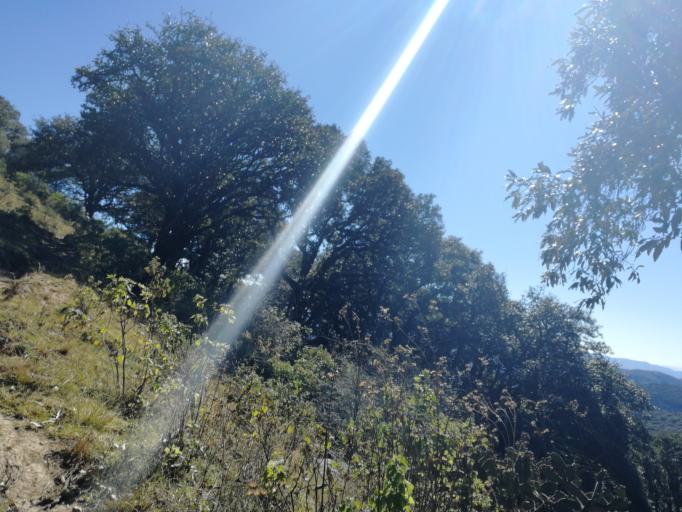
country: MX
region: San Luis Potosi
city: Zaragoza
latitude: 22.0087
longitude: -100.6161
